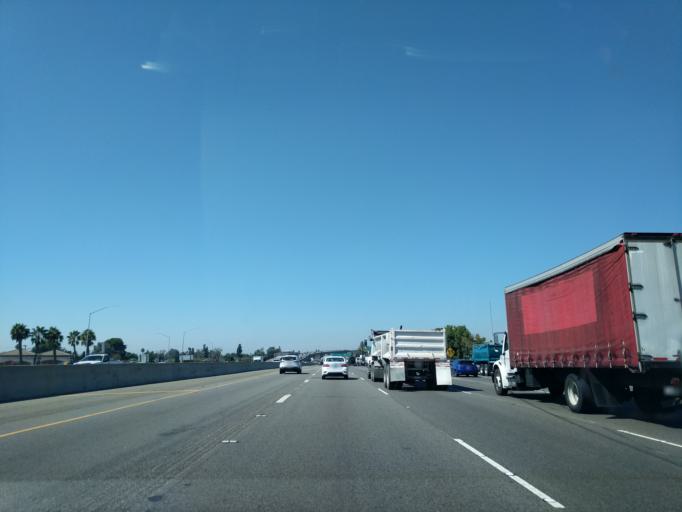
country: US
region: California
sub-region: Orange County
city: Tustin
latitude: 33.7375
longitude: -117.8239
